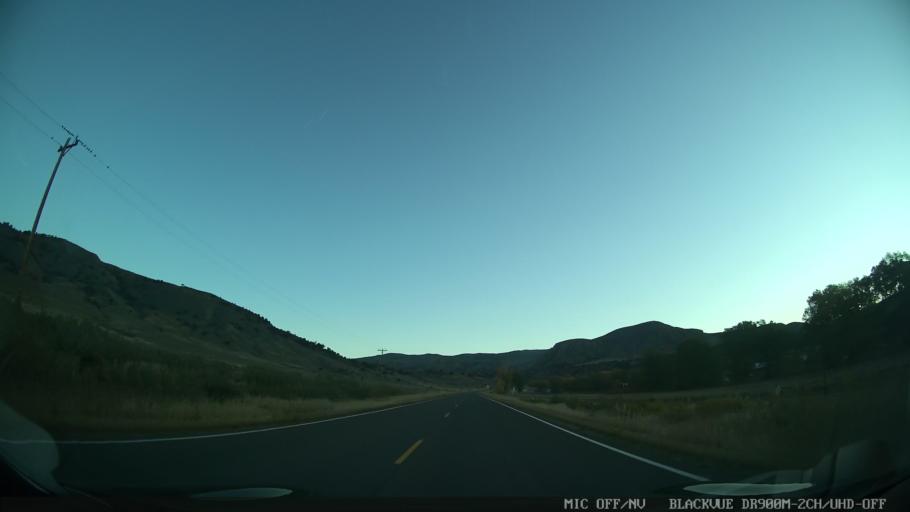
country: US
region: Colorado
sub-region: Eagle County
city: Edwards
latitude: 39.7473
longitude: -106.6759
